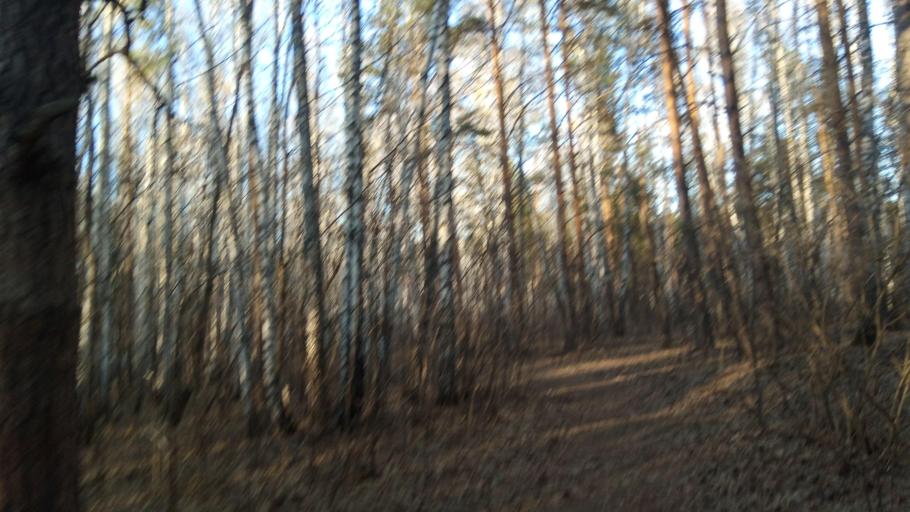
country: RU
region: Chelyabinsk
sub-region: Gorod Chelyabinsk
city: Chelyabinsk
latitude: 55.1441
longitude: 61.3421
